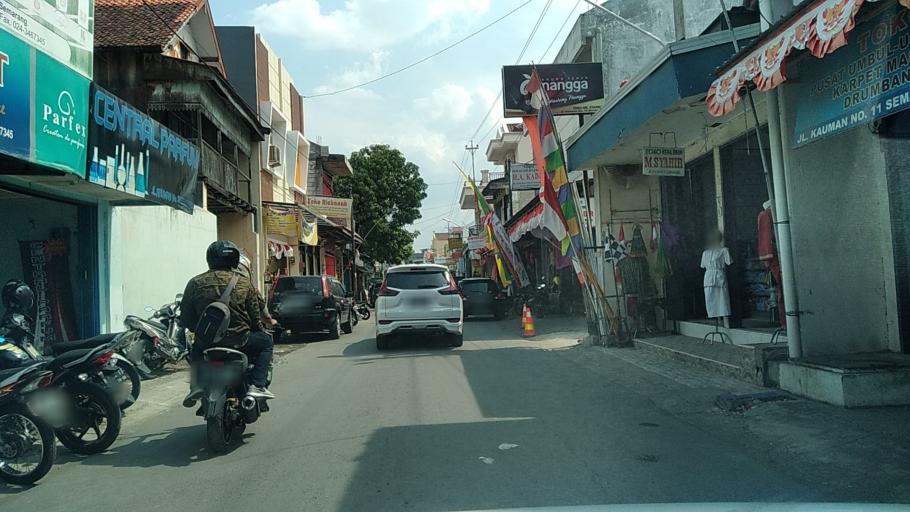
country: ID
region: Central Java
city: Semarang
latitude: -6.9732
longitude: 110.4226
